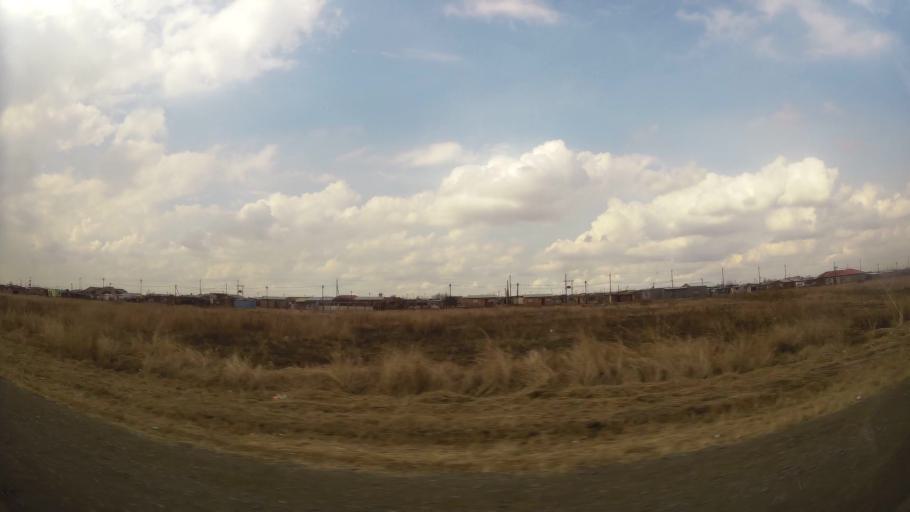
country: ZA
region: Orange Free State
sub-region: Fezile Dabi District Municipality
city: Sasolburg
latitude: -26.8528
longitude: 27.8888
